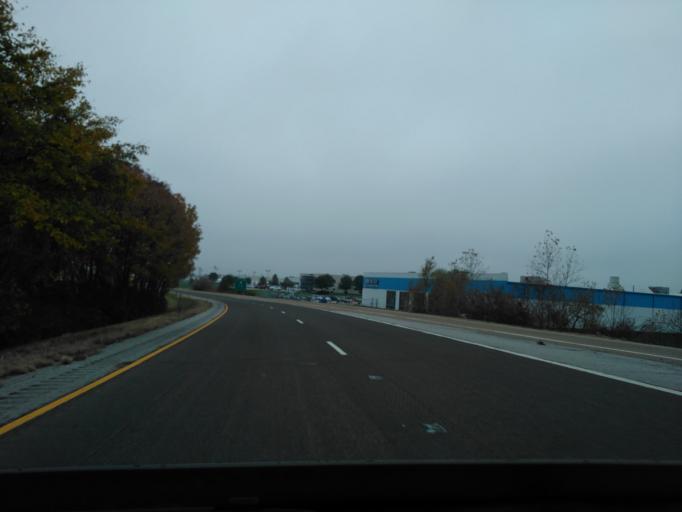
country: US
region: Illinois
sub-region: Madison County
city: Troy
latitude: 38.7470
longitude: -89.9095
